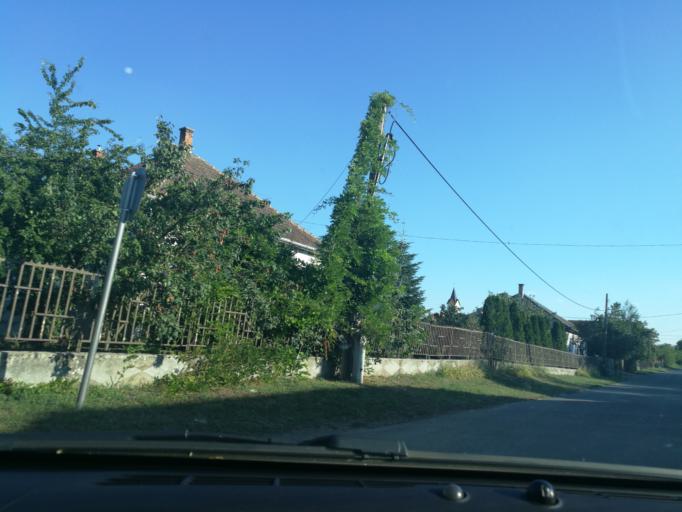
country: HU
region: Szabolcs-Szatmar-Bereg
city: Tiszabercel
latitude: 48.1620
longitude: 21.5990
